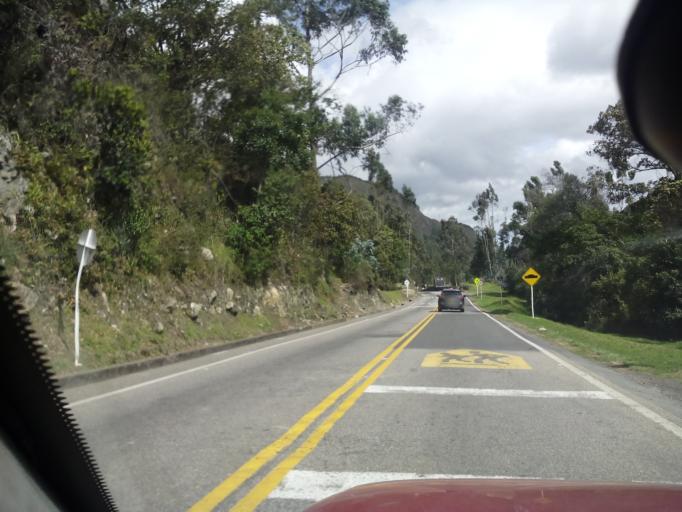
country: CO
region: Boyaca
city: Arcabuco
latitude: 5.7329
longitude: -73.4052
